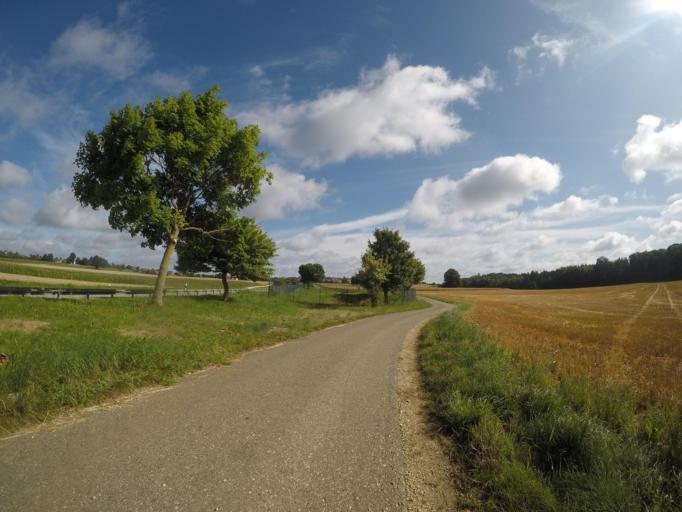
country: DE
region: Baden-Wuerttemberg
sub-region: Tuebingen Region
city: Laichingen
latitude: 48.4318
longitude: 9.6551
